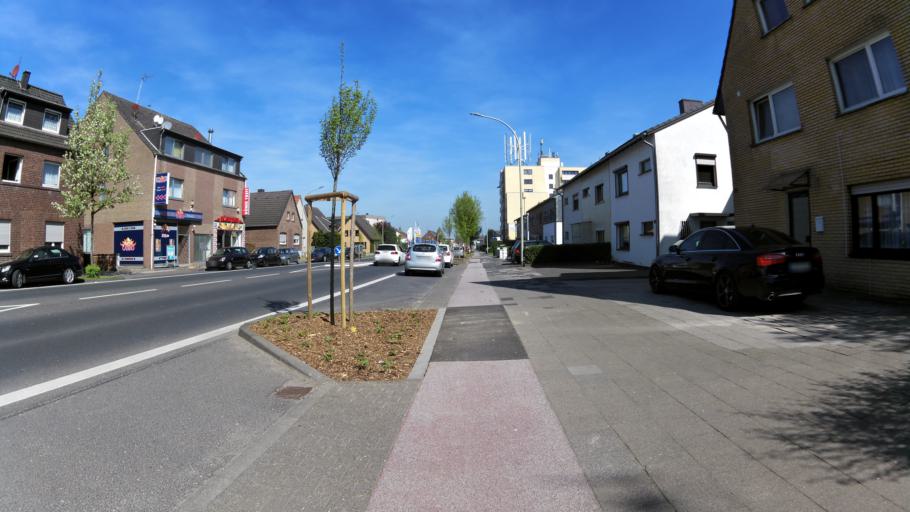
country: DE
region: North Rhine-Westphalia
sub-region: Regierungsbezirk Koln
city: Ubach-Palenberg
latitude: 50.9133
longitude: 6.1372
